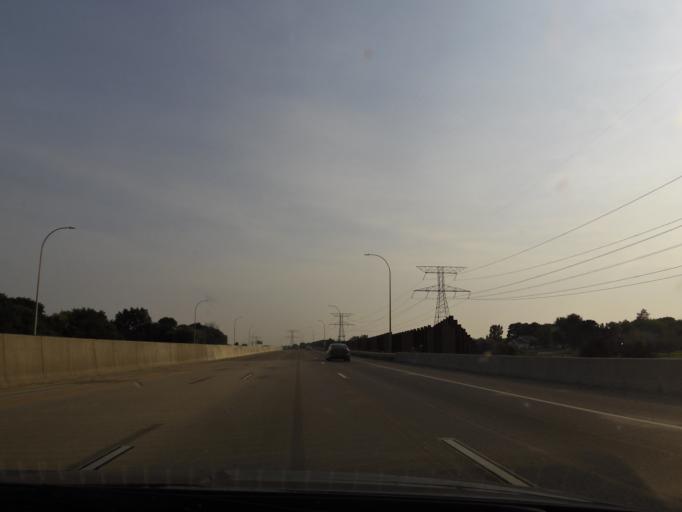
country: US
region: Minnesota
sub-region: Hennepin County
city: Maple Grove
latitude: 45.0606
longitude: -93.4503
